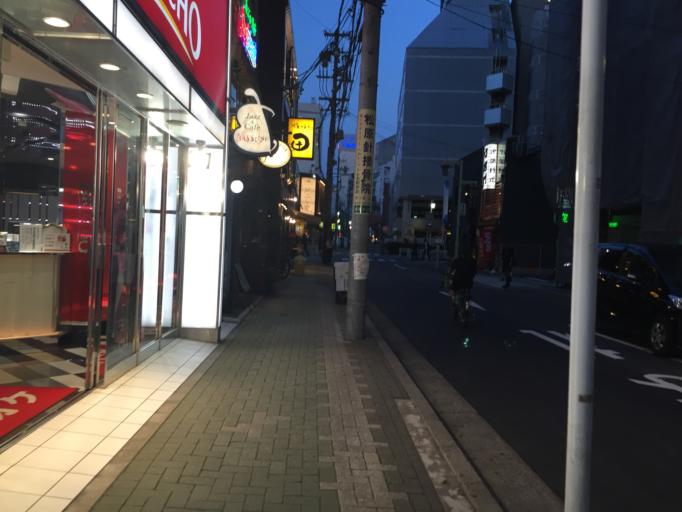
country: JP
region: Aichi
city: Nagoya-shi
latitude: 35.1726
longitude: 136.8851
